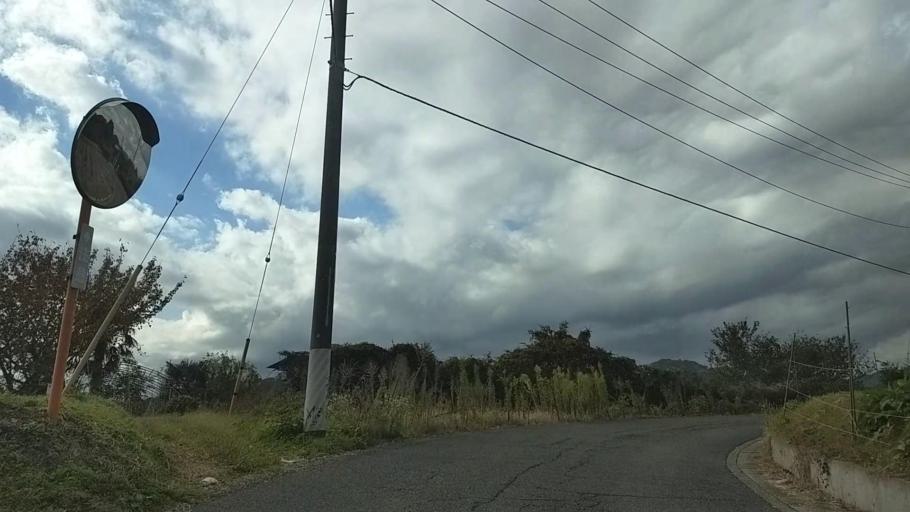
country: JP
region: Kanagawa
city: Hadano
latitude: 35.3516
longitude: 139.1737
